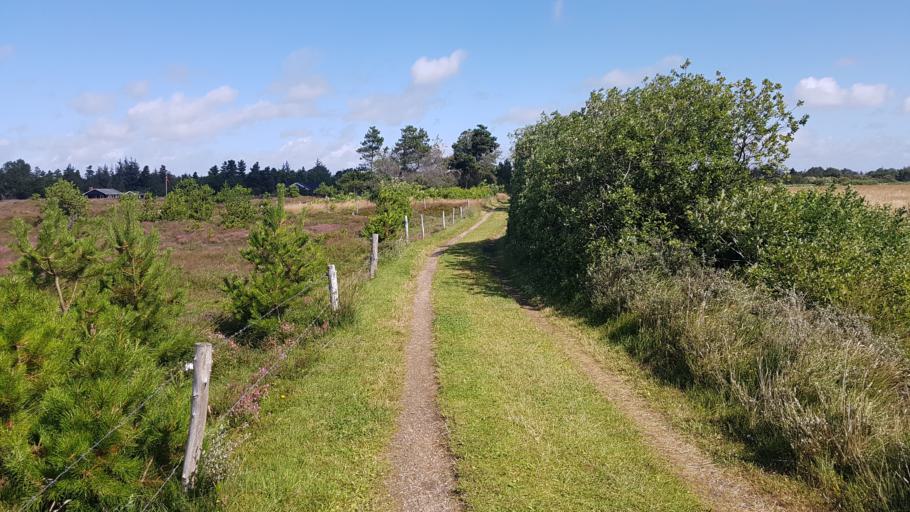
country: DE
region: Schleswig-Holstein
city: List
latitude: 55.1252
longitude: 8.5387
